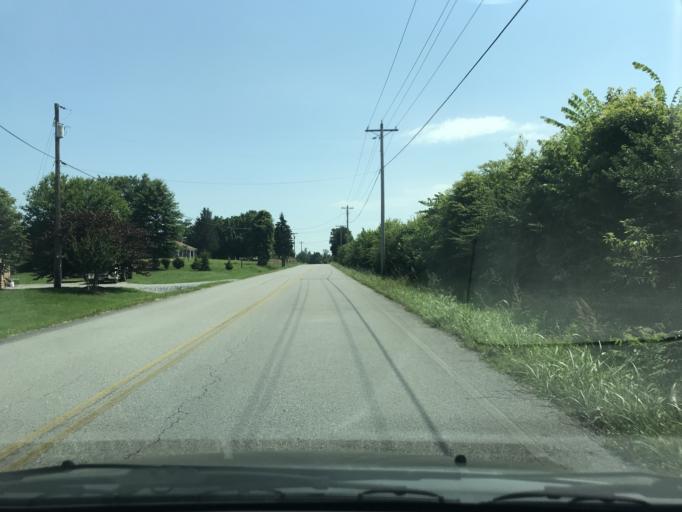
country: US
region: Tennessee
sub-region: Loudon County
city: Lenoir City
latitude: 35.8217
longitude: -84.3285
